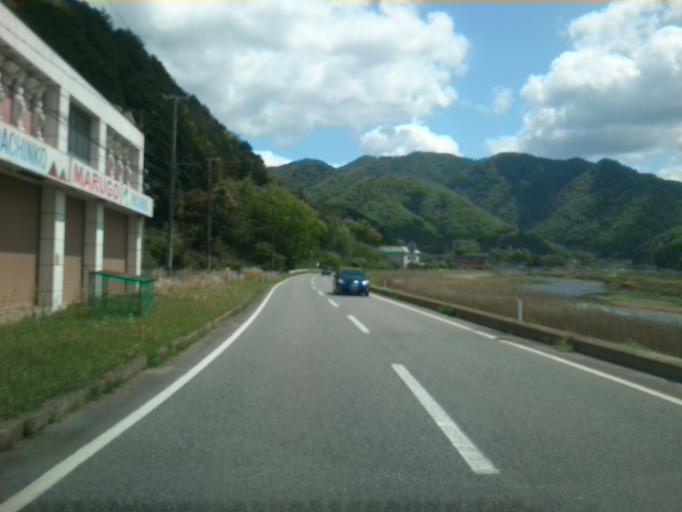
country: JP
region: Hyogo
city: Toyooka
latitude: 35.4556
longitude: 134.8712
